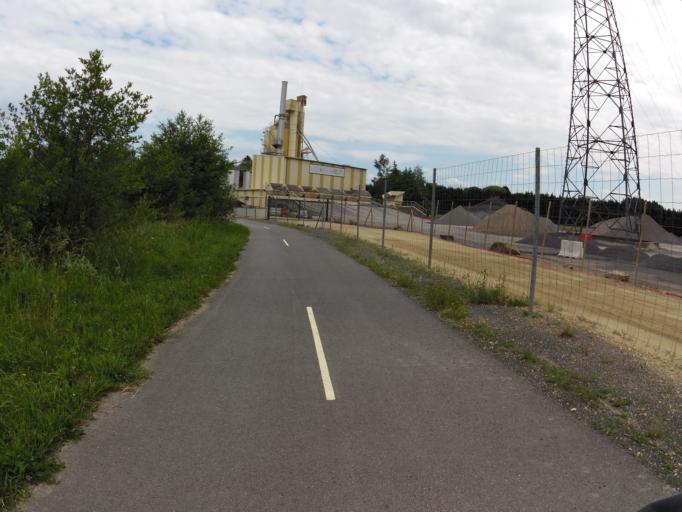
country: FR
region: Champagne-Ardenne
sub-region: Departement des Ardennes
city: Lumes
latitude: 49.7437
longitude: 4.7788
